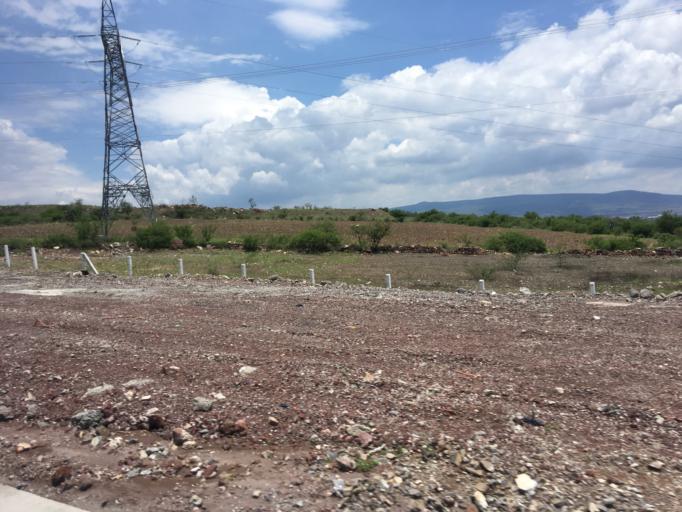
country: MX
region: Guanajuato
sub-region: Apaseo el Grande
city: Coachiti
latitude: 20.5141
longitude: -100.6028
